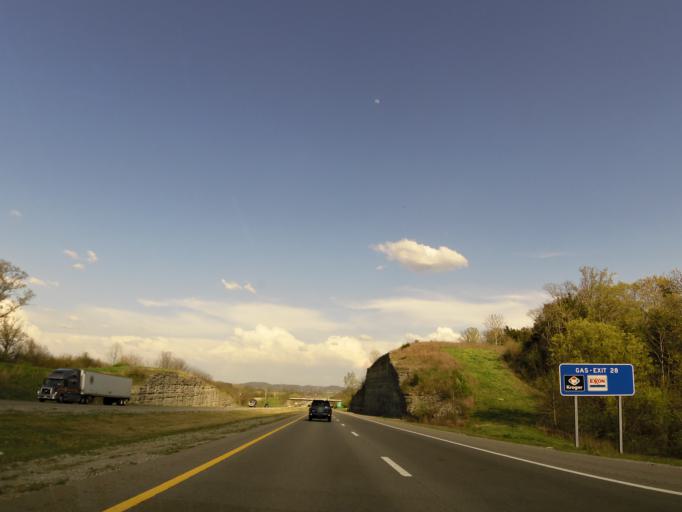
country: US
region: Tennessee
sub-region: Williamson County
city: Thompson's Station
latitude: 35.8229
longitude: -86.9201
